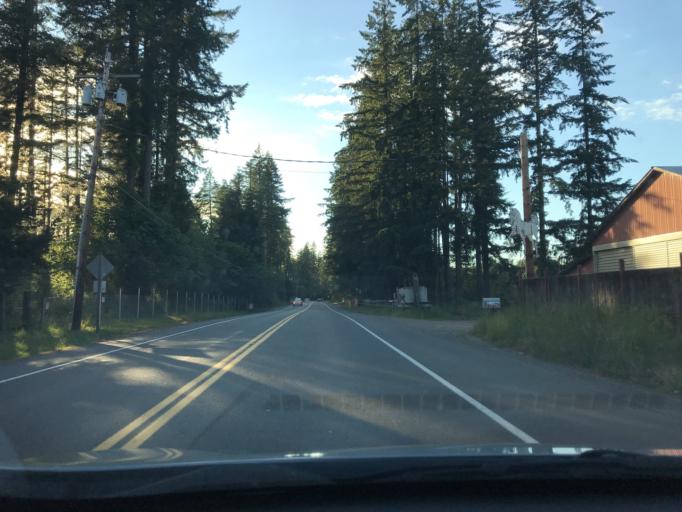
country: US
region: Washington
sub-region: King County
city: Lake Morton-Berrydale
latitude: 47.2989
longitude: -122.0838
